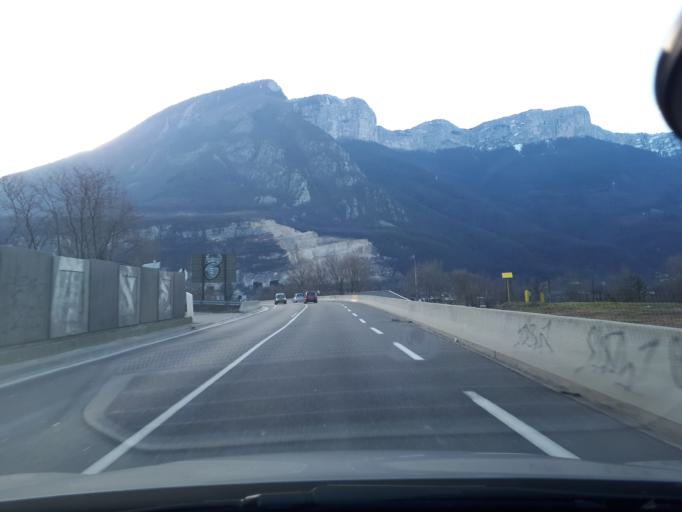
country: FR
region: Rhone-Alpes
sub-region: Departement de l'Isere
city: Fontanil-Cornillon
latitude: 45.2357
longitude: 5.6569
